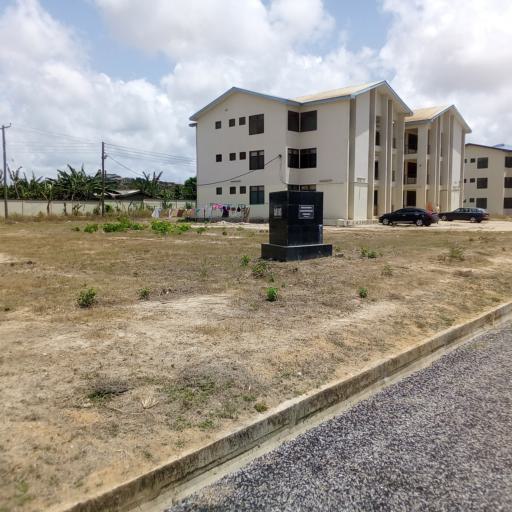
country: GH
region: Central
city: Cape Coast
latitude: 5.1332
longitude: -1.2956
